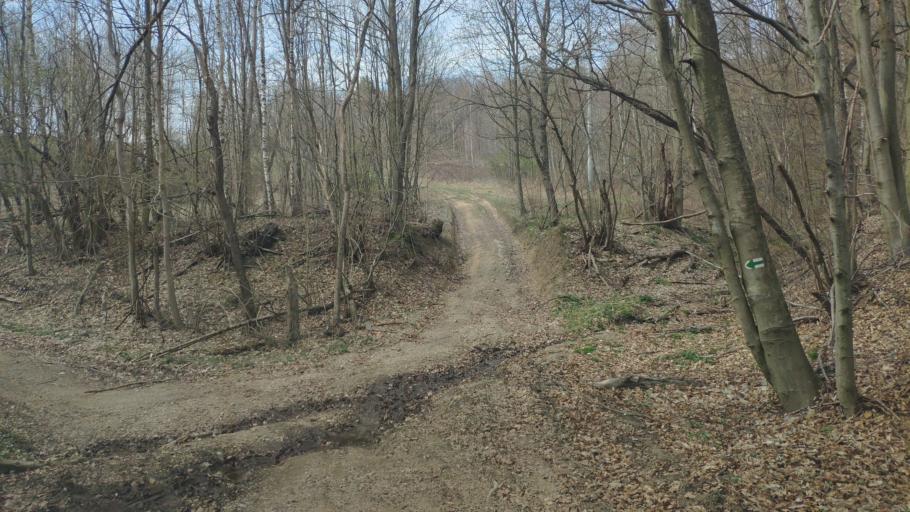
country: SK
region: Kosicky
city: Moldava nad Bodvou
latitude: 48.7484
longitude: 21.0236
